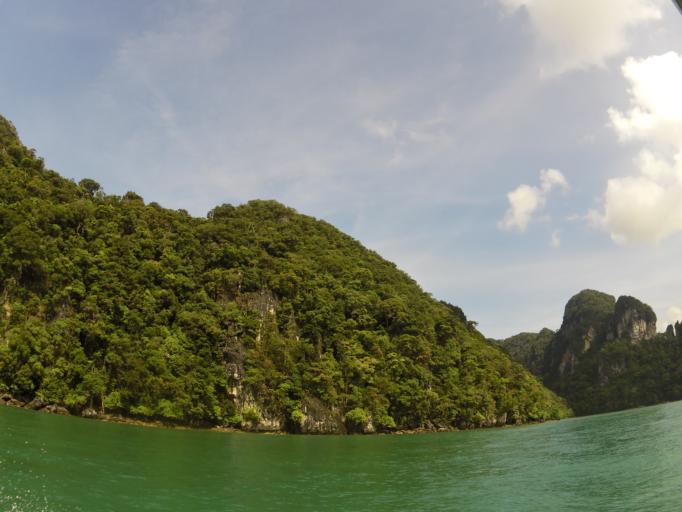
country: MY
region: Kedah
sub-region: Langkawi
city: Kuah
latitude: 6.2036
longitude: 99.7783
